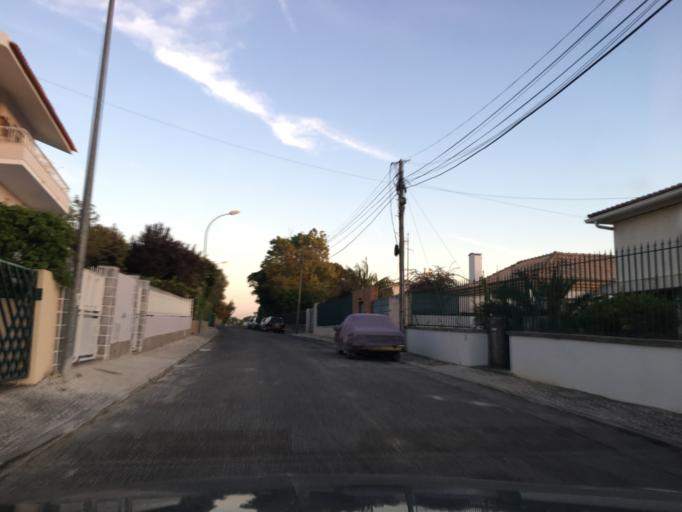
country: PT
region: Lisbon
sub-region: Oeiras
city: Paco de Arcos
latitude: 38.7011
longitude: -9.2896
